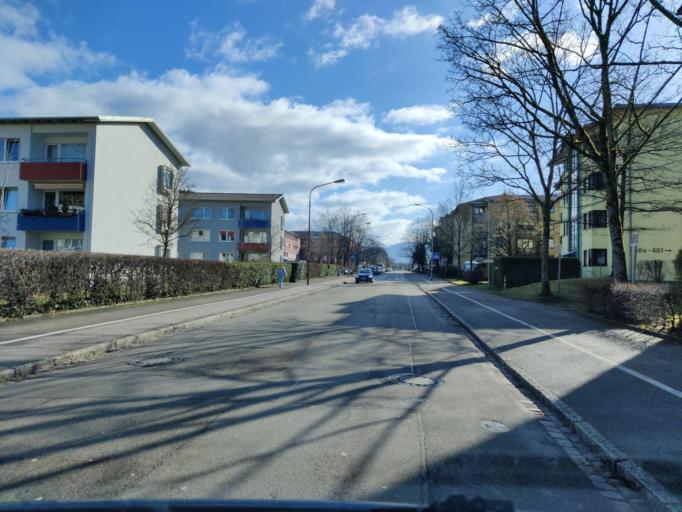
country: DE
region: Baden-Wuerttemberg
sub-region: Freiburg Region
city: Freiburg
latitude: 47.9816
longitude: 7.9007
